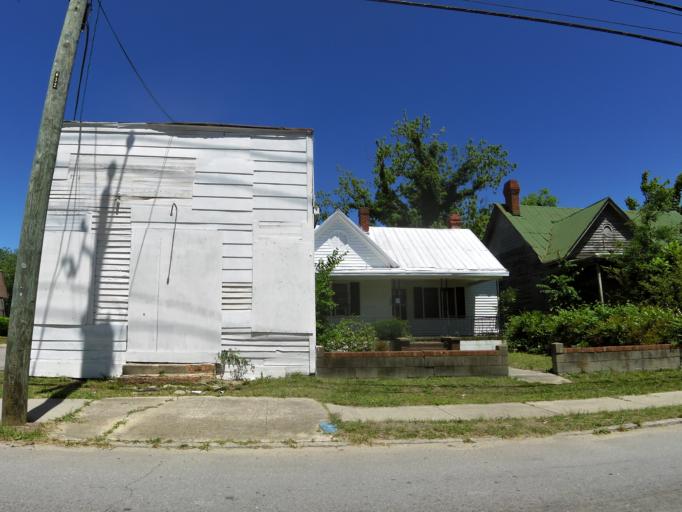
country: US
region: Georgia
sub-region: Richmond County
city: Augusta
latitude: 33.4556
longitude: -81.9848
